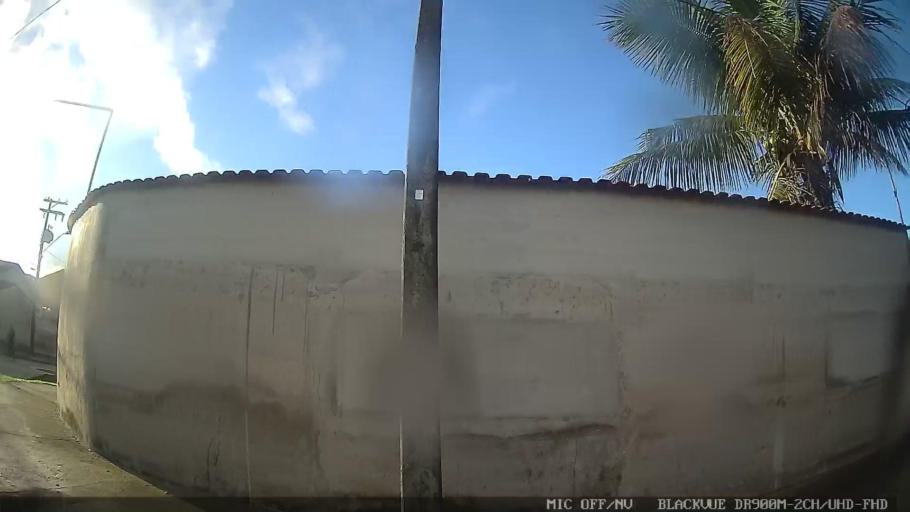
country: BR
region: Sao Paulo
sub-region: Itanhaem
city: Itanhaem
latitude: -24.2354
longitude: -46.8834
